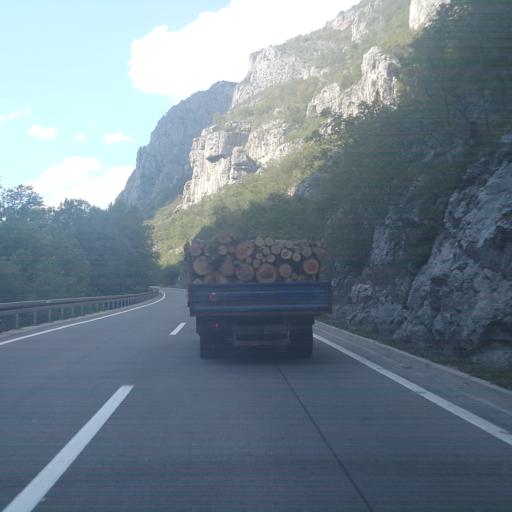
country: RS
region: Central Serbia
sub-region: Nisavski Okrug
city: Svrljig
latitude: 43.3313
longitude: 22.1538
